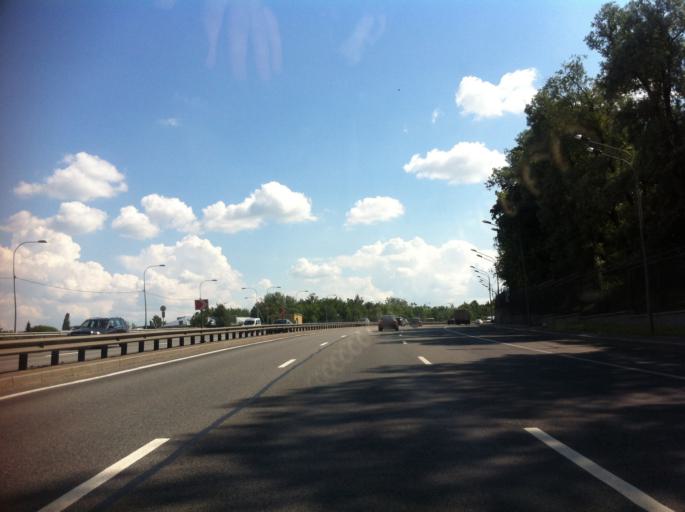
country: RU
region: St.-Petersburg
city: Aleksandrovskaya
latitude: 59.7729
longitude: 30.3313
